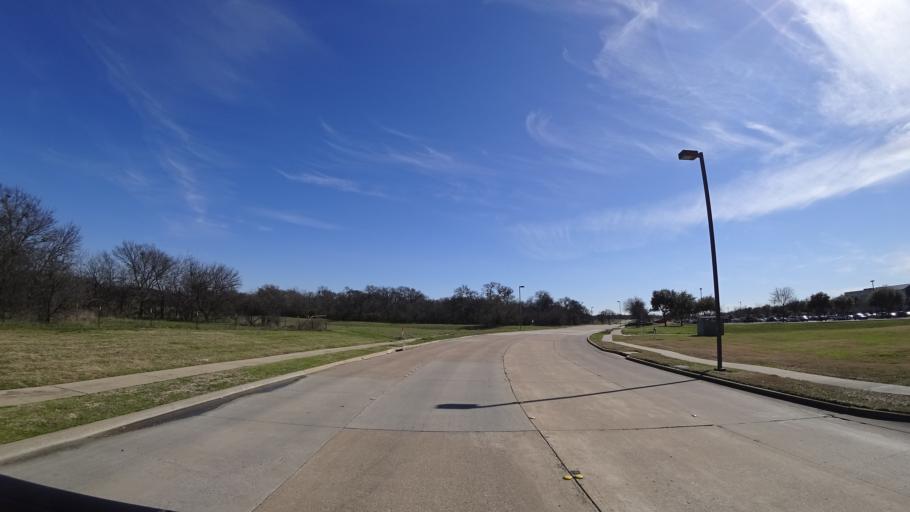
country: US
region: Texas
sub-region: Denton County
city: Lewisville
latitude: 32.9941
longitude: -96.9604
